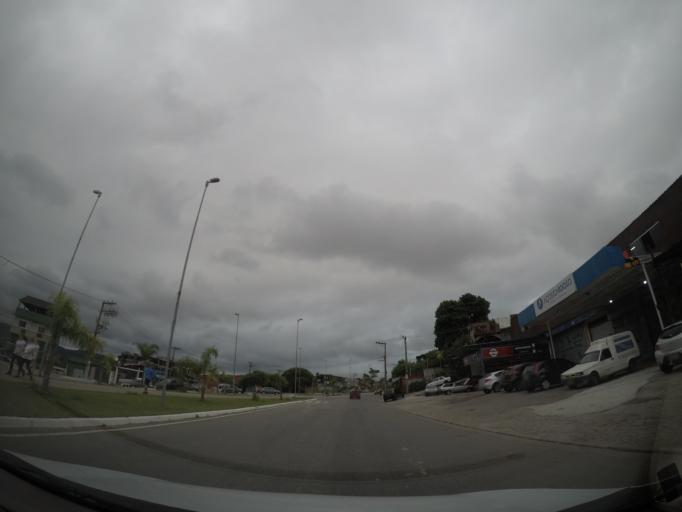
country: BR
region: Sao Paulo
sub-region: Guarulhos
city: Guarulhos
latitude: -23.4100
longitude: -46.4520
